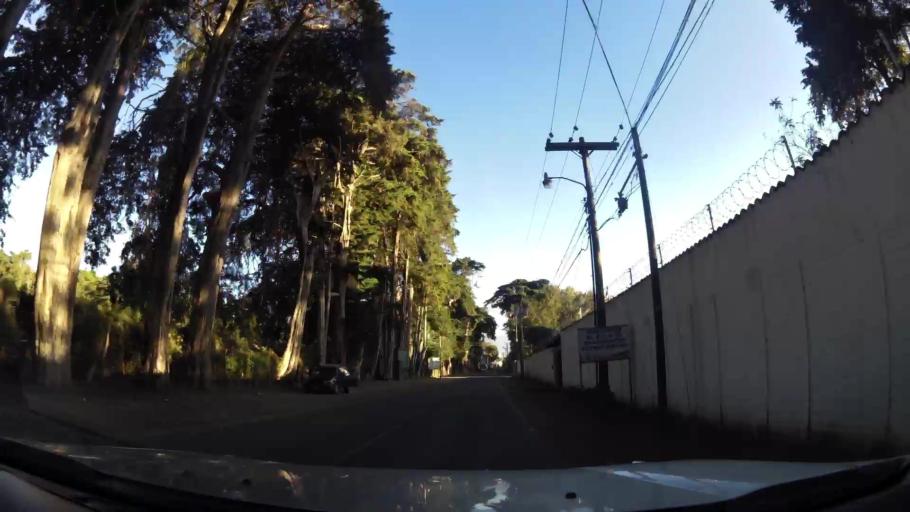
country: GT
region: Sacatepequez
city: San Lucas Sacatepequez
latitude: 14.6163
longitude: -90.6586
